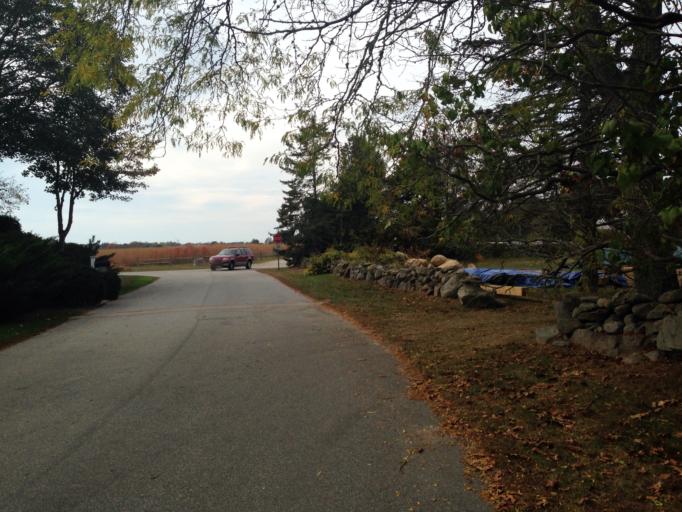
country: US
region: Connecticut
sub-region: New London County
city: Pawcatuck
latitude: 41.3325
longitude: -71.8340
